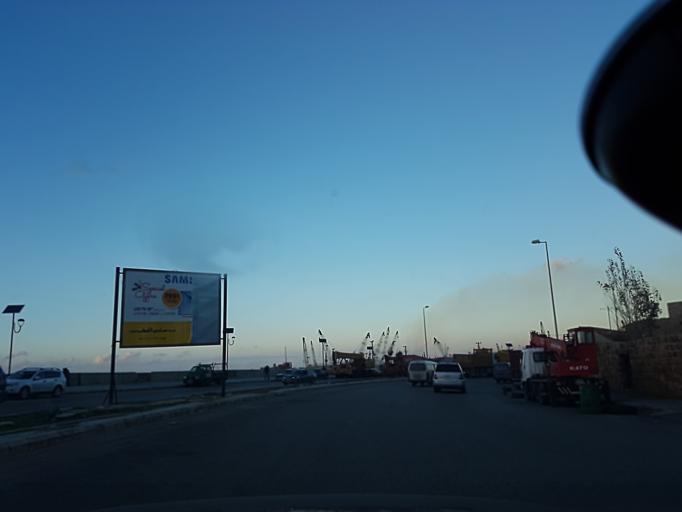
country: LB
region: Liban-Sud
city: Sidon
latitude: 33.5625
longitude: 35.3668
